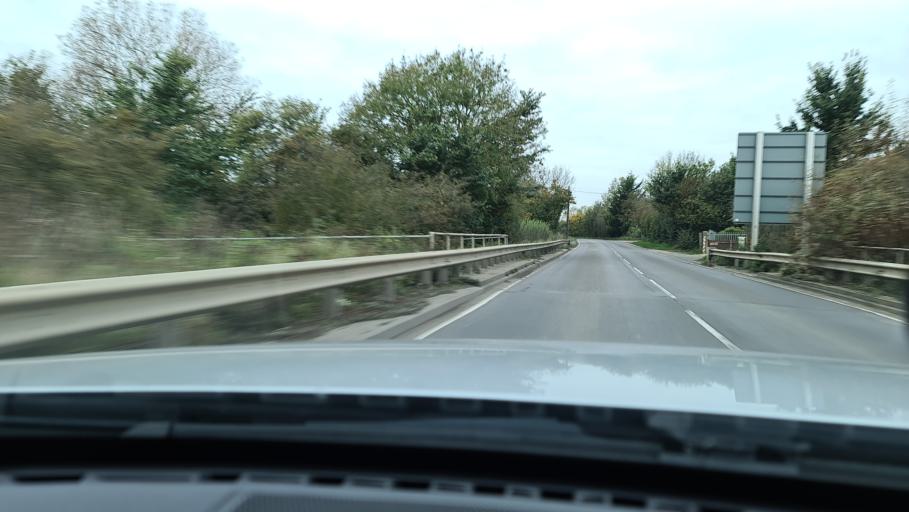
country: GB
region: England
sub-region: Buckinghamshire
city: Waddesdon
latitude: 51.8565
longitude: -0.9757
